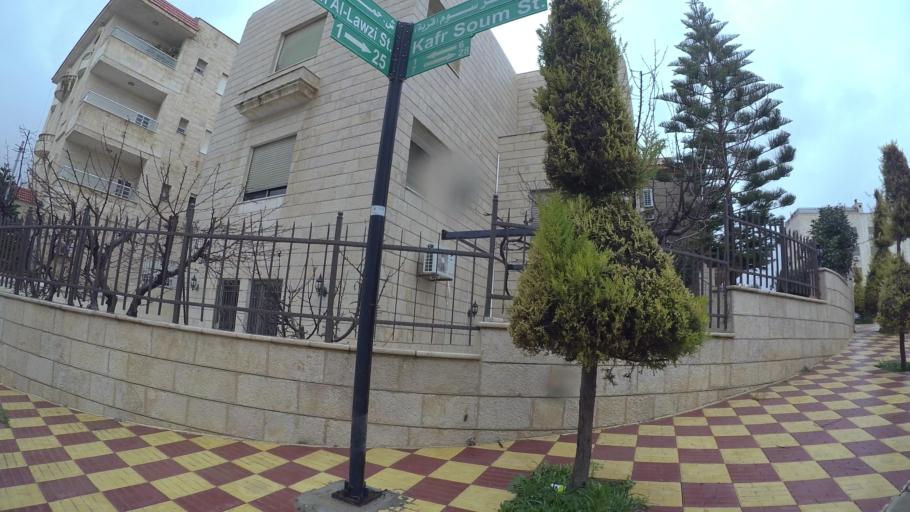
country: JO
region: Amman
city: Al Jubayhah
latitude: 32.0348
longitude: 35.8858
